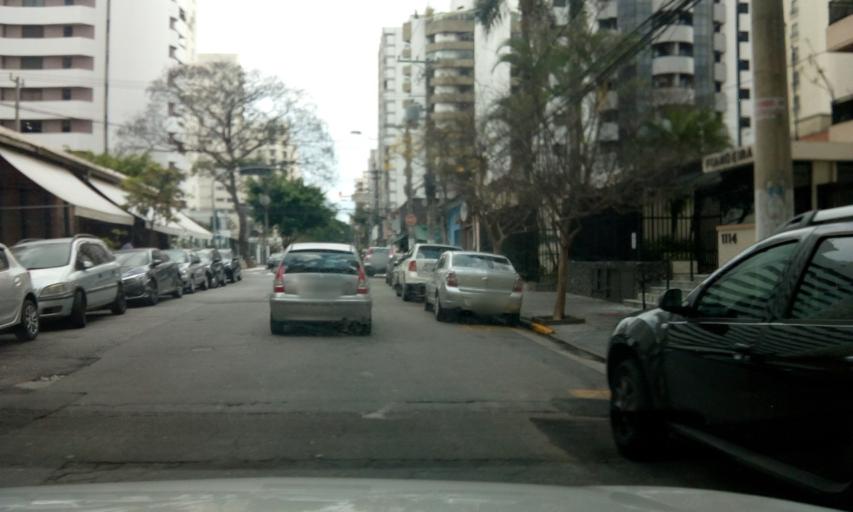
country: BR
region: Sao Paulo
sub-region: Sao Paulo
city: Sao Paulo
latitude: -23.6087
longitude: -46.6595
